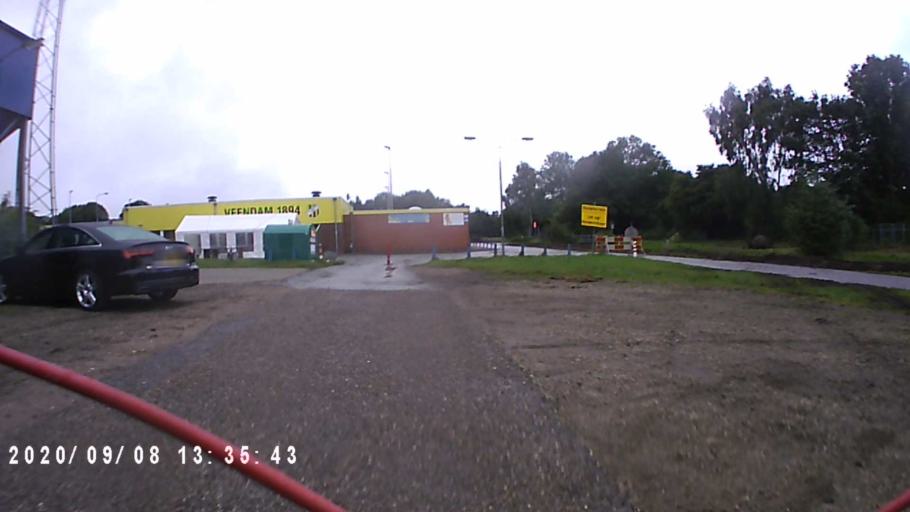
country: NL
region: Groningen
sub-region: Gemeente Veendam
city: Veendam
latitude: 53.1095
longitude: 6.8646
